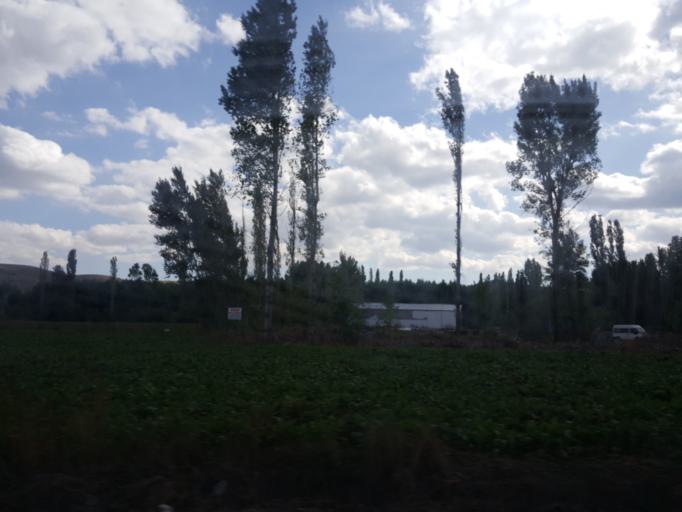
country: TR
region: Tokat
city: Yesilyurt
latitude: 40.0254
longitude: 36.2918
